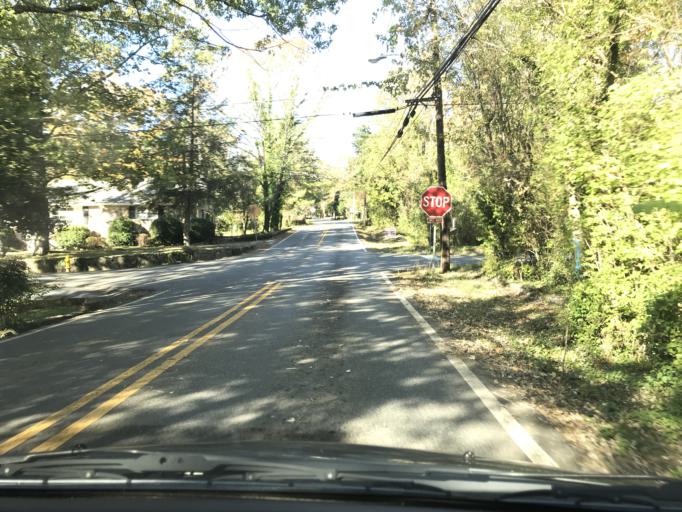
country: US
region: Georgia
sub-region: Walker County
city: Lookout Mountain
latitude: 34.9762
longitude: -85.3539
